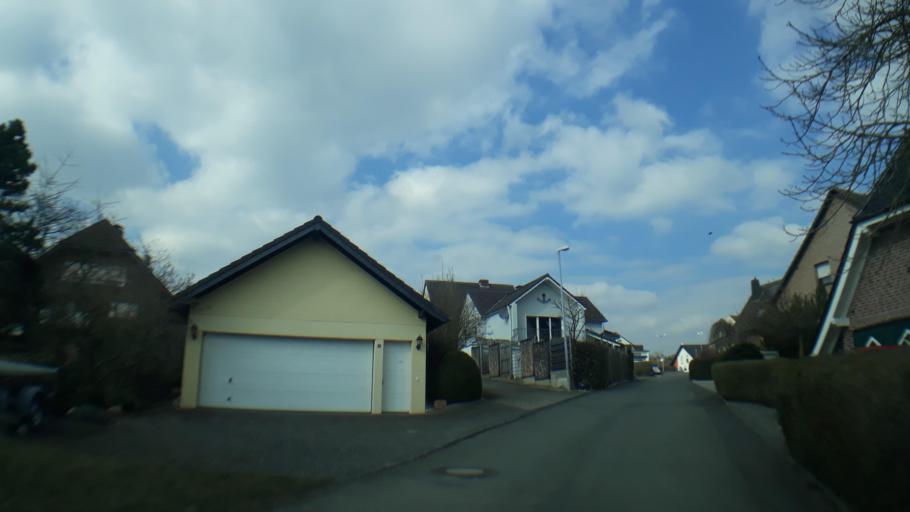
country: DE
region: Rheinland-Pfalz
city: Berg
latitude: 50.5520
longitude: 6.9465
